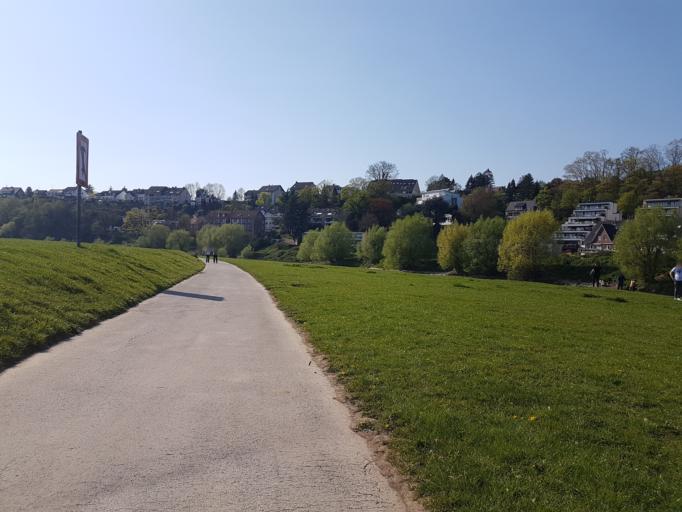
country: DE
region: North Rhine-Westphalia
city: Hattingen
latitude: 51.4053
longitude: 7.1676
